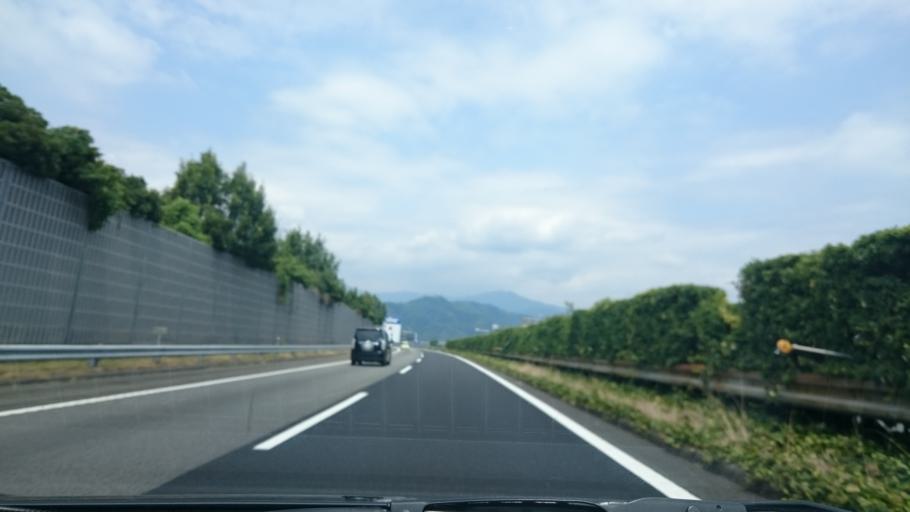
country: JP
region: Shizuoka
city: Shizuoka-shi
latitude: 34.9907
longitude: 138.4357
